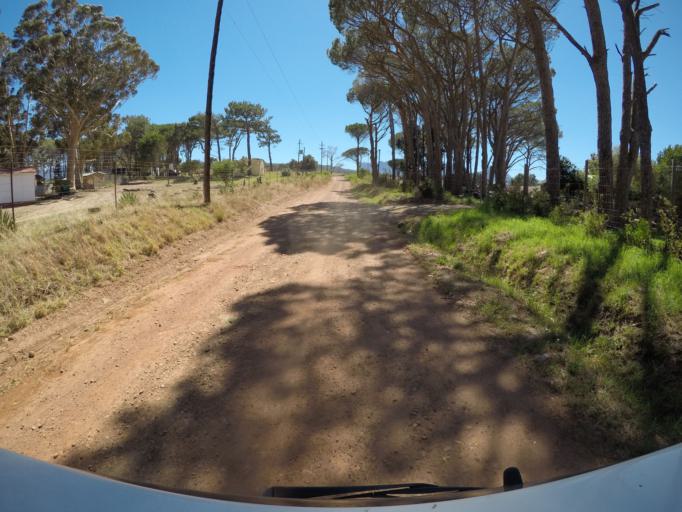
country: ZA
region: Western Cape
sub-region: Overberg District Municipality
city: Grabouw
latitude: -34.1158
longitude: 18.8787
